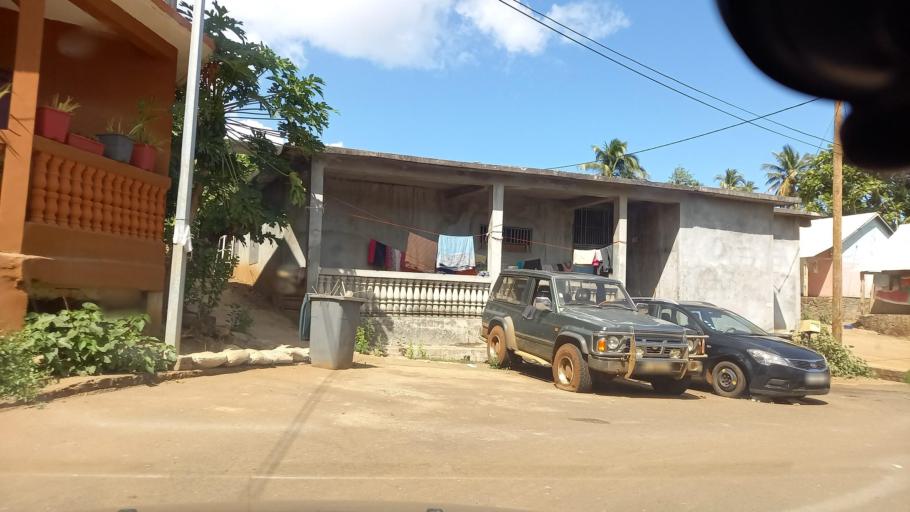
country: YT
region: M'Tsangamouji
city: M'Tsangamouji
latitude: -12.7634
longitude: 45.0747
